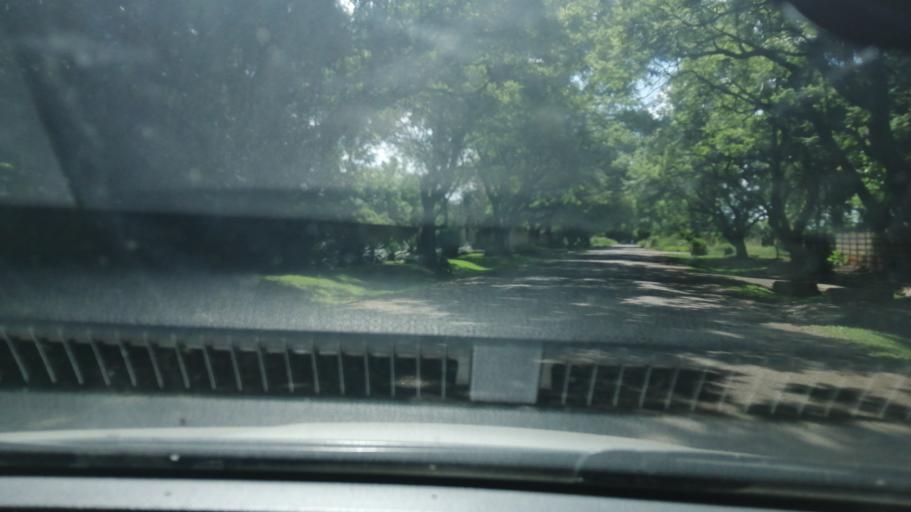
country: ZW
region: Harare
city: Harare
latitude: -17.7559
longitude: 31.0739
